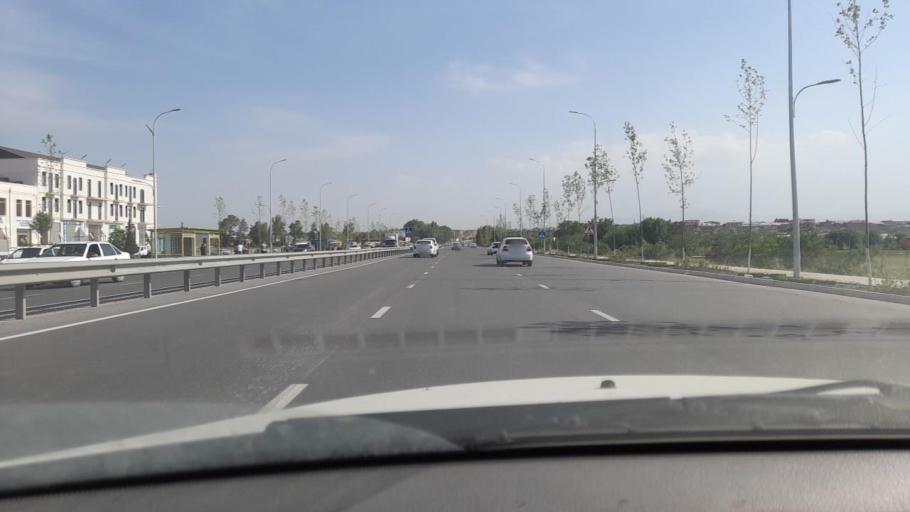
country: UZ
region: Samarqand
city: Samarqand
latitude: 39.7102
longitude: 66.9497
